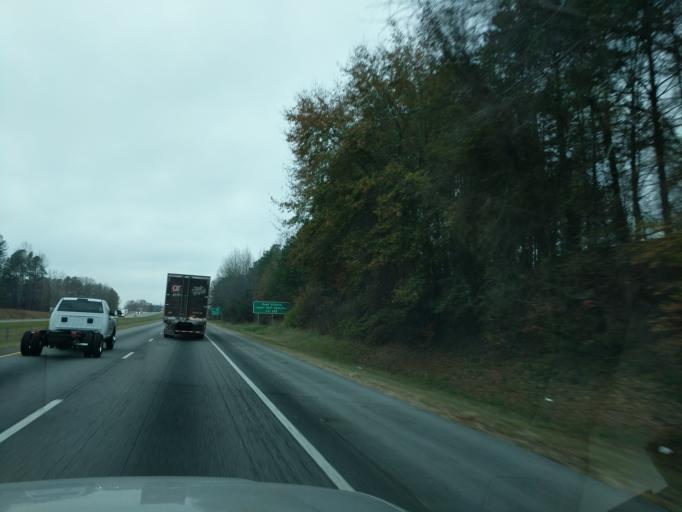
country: US
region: Georgia
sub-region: Jackson County
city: Braselton
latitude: 34.1214
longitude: -83.7520
